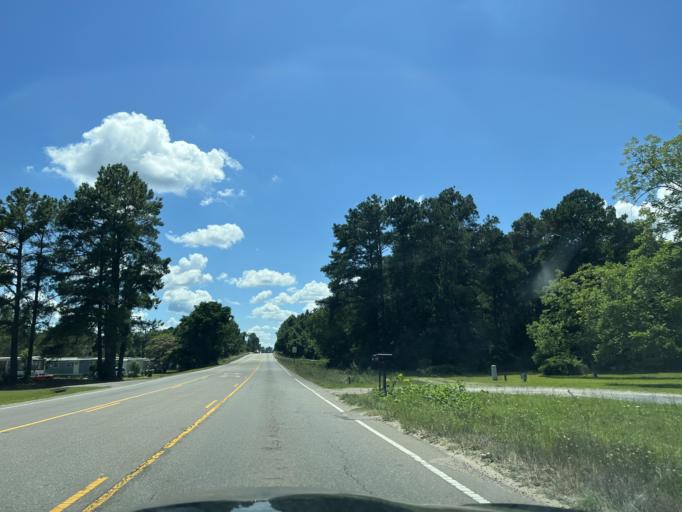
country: US
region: North Carolina
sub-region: Lee County
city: Sanford
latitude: 35.4446
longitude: -79.1742
